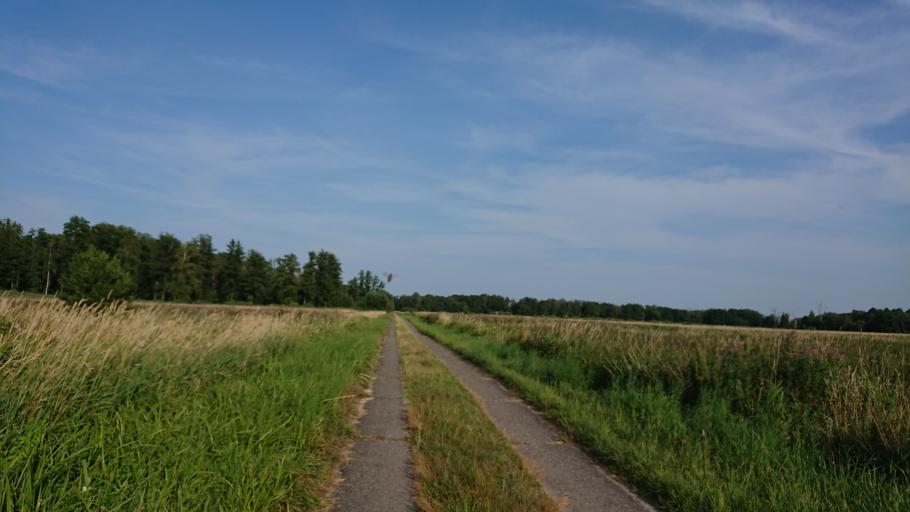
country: DE
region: Mecklenburg-Vorpommern
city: Gormin
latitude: 53.9739
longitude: 13.2917
